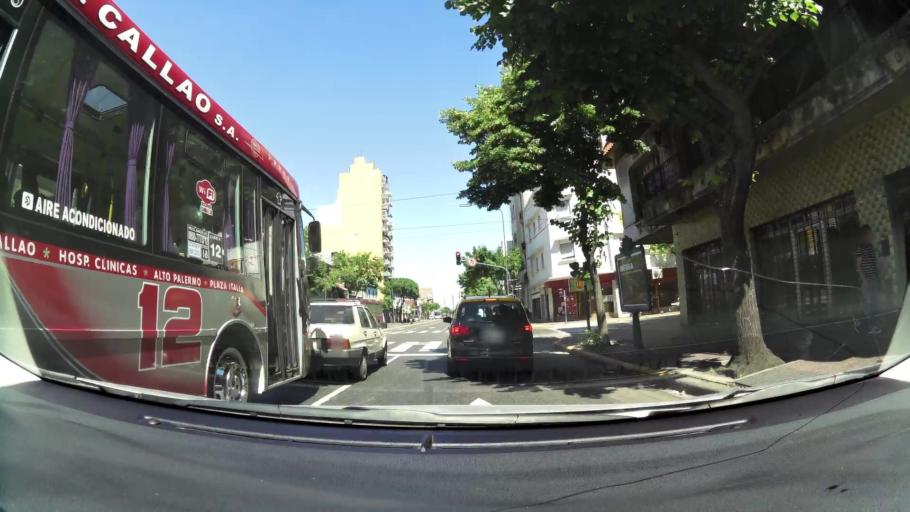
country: AR
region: Buenos Aires F.D.
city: Buenos Aires
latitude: -34.6271
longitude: -58.3855
